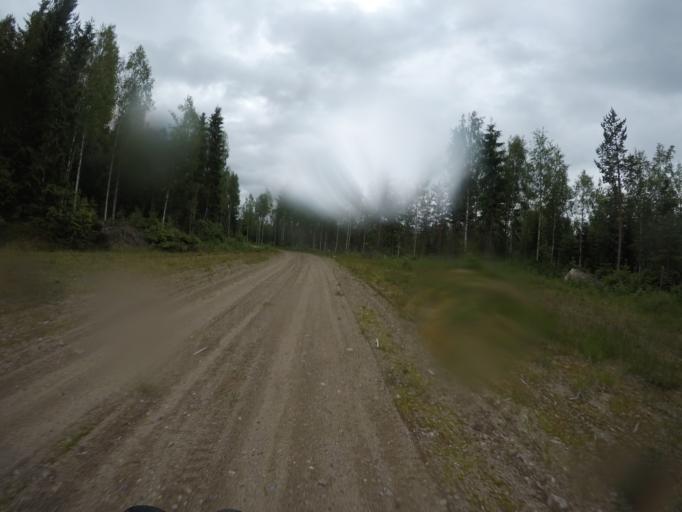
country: SE
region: Dalarna
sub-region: Ludvika Kommun
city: Abborrberget
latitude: 60.0562
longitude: 14.5692
